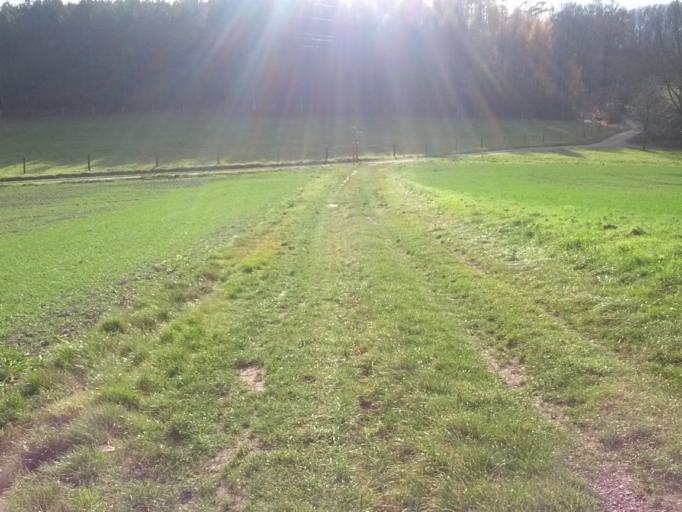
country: DE
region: Thuringia
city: Krauthausen
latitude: 50.9934
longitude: 10.2287
